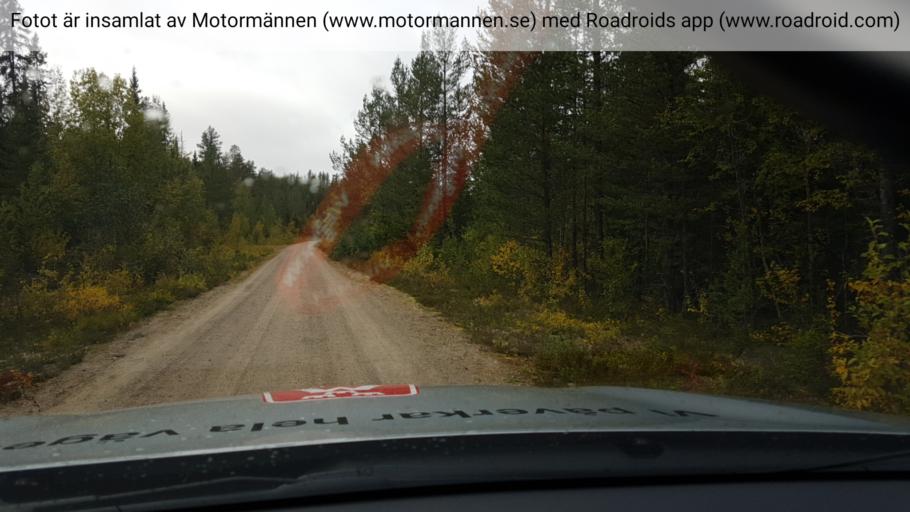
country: SE
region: Jaemtland
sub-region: Harjedalens Kommun
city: Sveg
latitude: 62.2471
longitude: 13.2993
